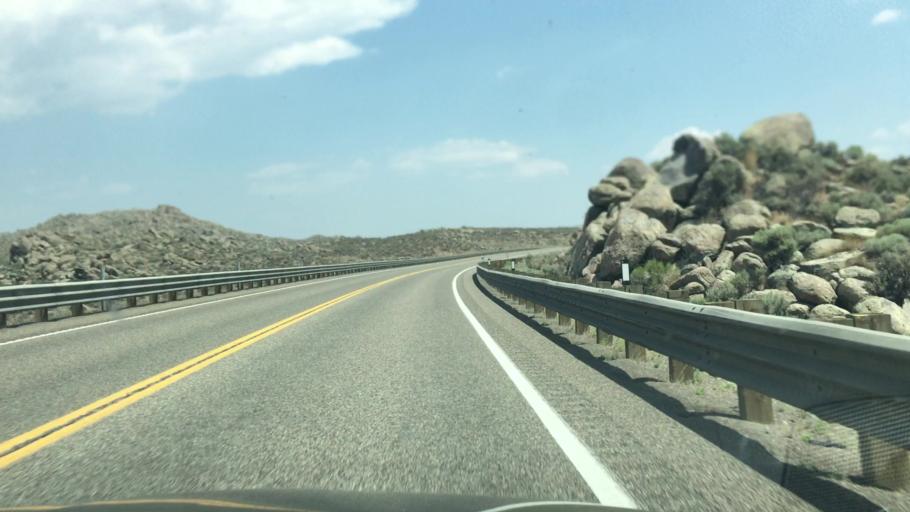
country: US
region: Nevada
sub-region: Elko County
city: Jackpot
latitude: 41.7359
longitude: -114.7872
